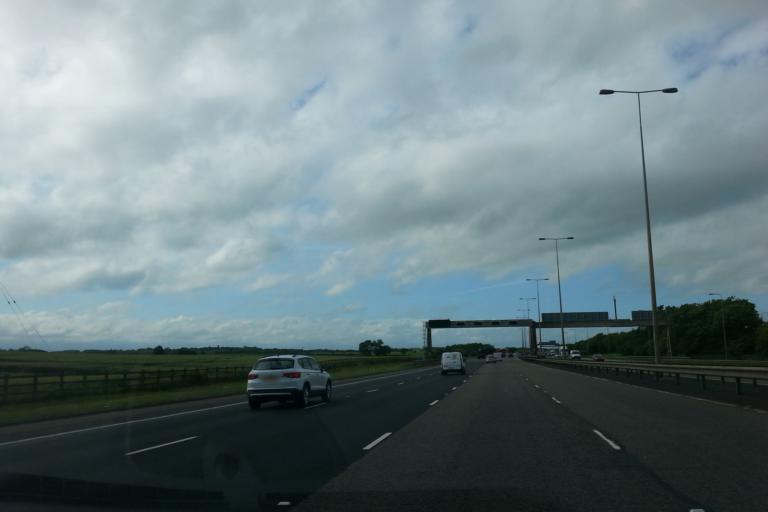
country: GB
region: England
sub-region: Cambridgeshire
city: Sawtry
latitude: 52.4458
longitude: -0.2763
